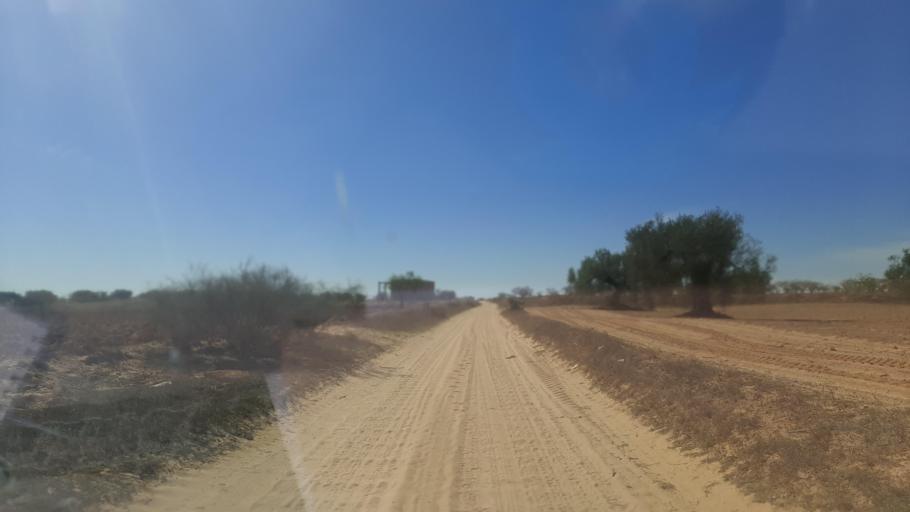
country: TN
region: Safaqis
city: Sfax
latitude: 34.8161
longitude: 10.5490
